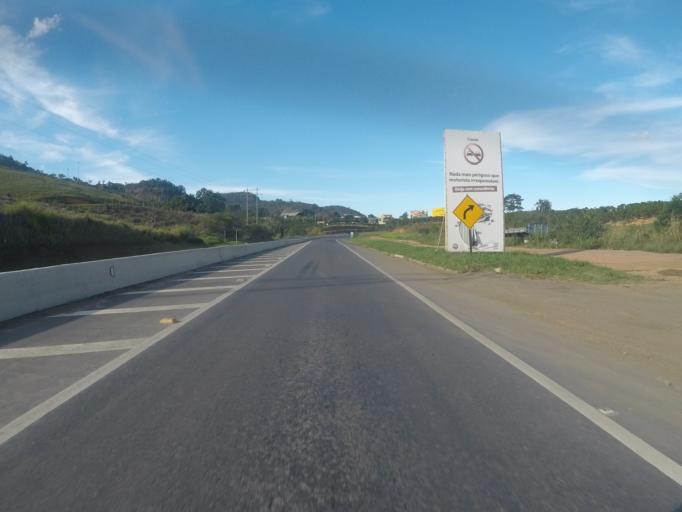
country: BR
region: Espirito Santo
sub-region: Ibiracu
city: Ibiracu
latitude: -19.8646
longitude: -40.3936
